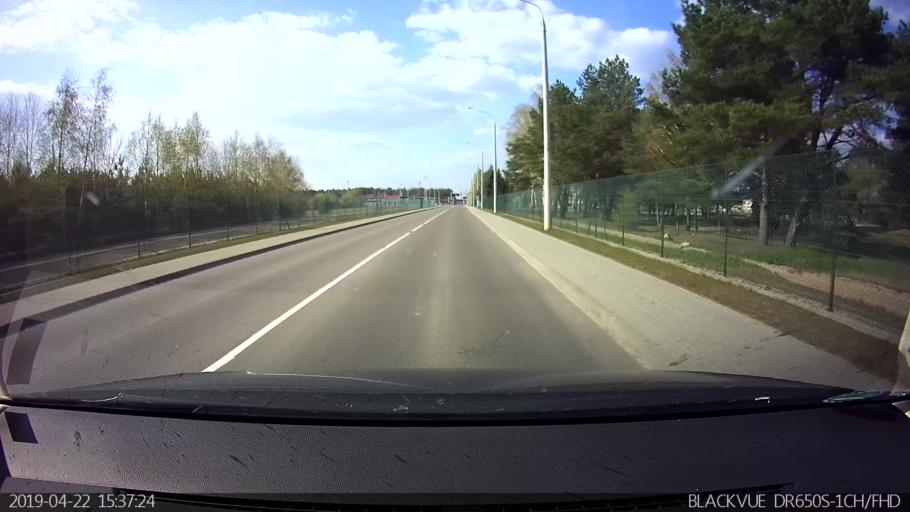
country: PL
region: Podlasie
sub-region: Powiat hajnowski
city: Czeremcha
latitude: 52.4626
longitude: 23.3629
